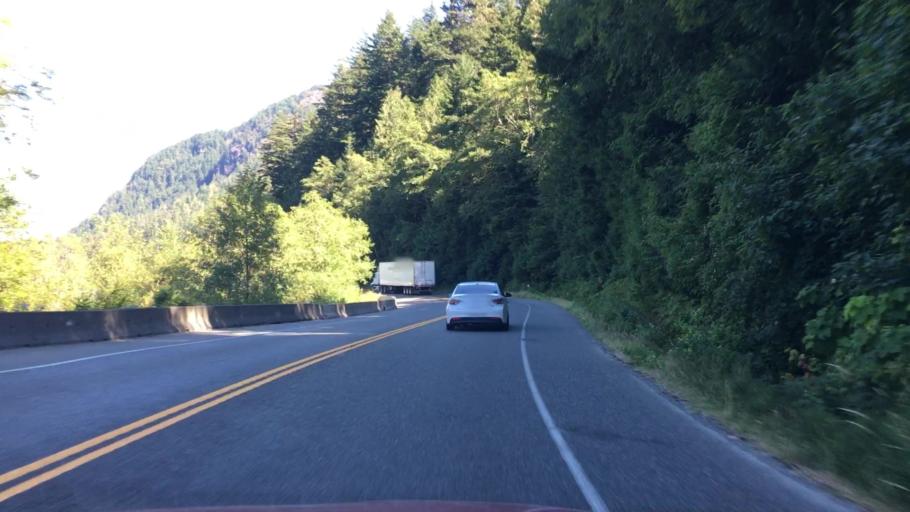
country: CA
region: British Columbia
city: Port Alberni
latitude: 49.2894
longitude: -124.6426
